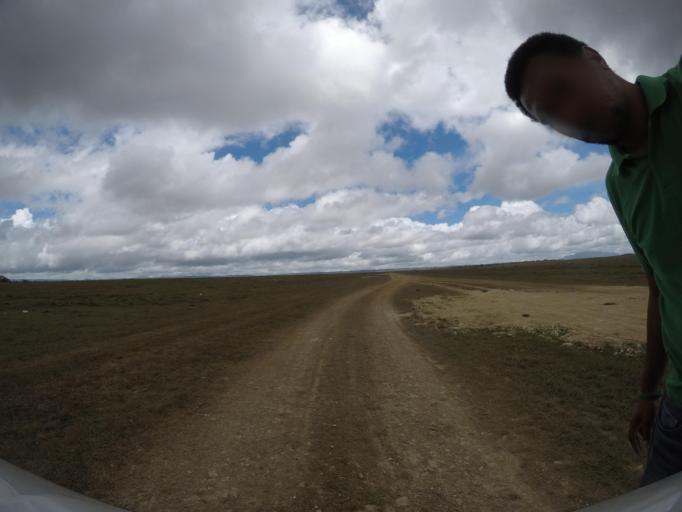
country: TL
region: Lautem
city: Lospalos
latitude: -8.4483
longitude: 126.9873
